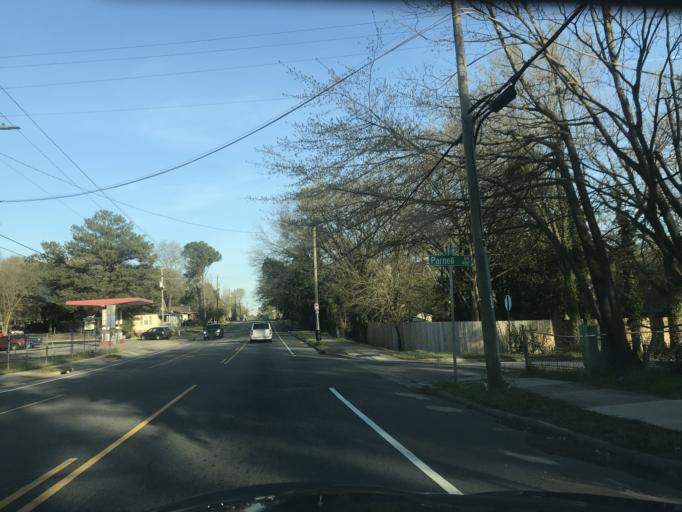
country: US
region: North Carolina
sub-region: Wake County
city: Raleigh
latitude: 35.7760
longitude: -78.6093
